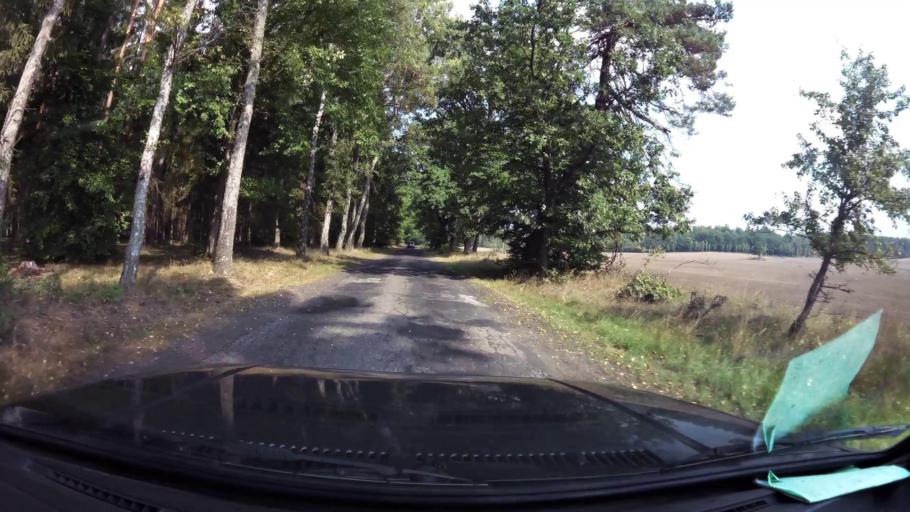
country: PL
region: West Pomeranian Voivodeship
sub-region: Powiat koszalinski
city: Bobolice
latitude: 54.0933
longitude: 16.4868
